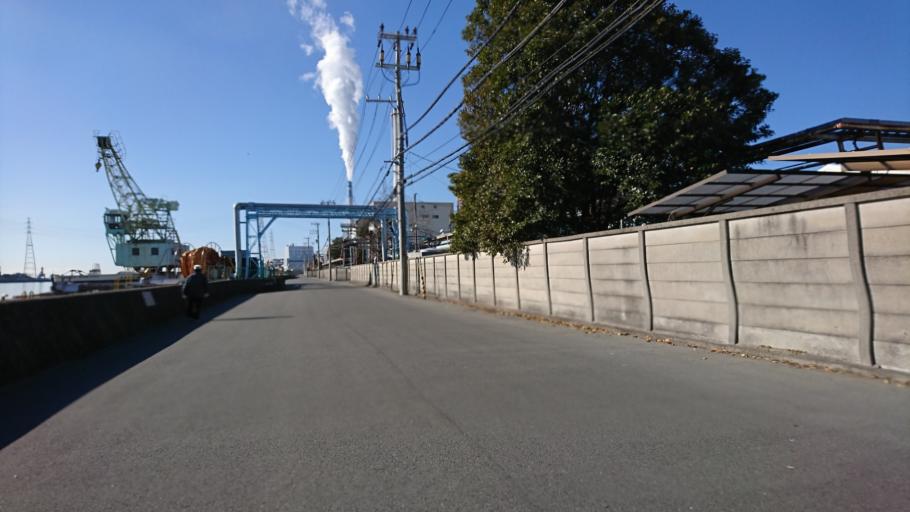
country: JP
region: Hyogo
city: Kakogawacho-honmachi
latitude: 34.7606
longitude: 134.7731
